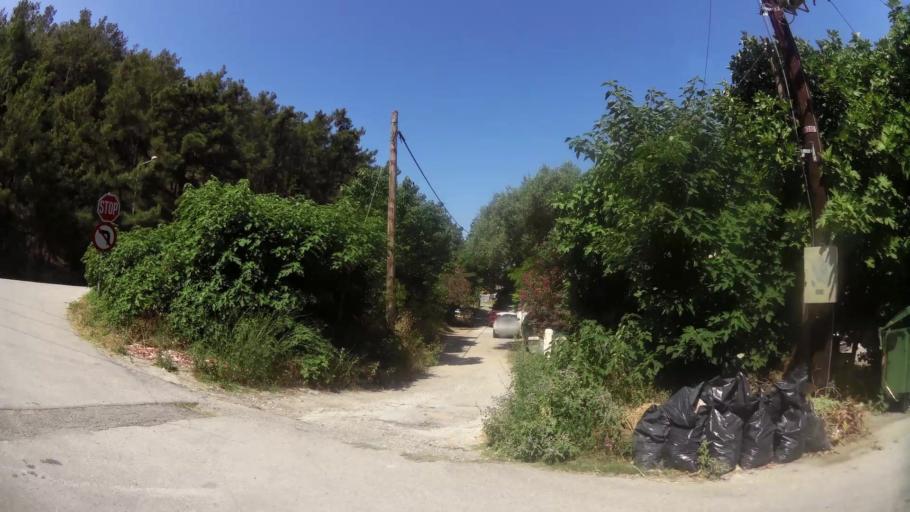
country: GR
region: Central Macedonia
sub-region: Nomos Thessalonikis
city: Agia Triada
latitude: 40.4991
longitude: 22.8791
